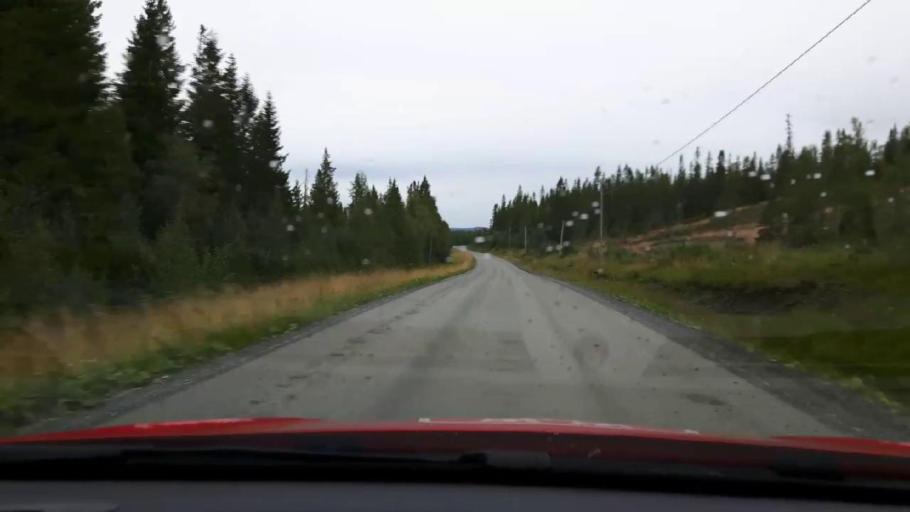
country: SE
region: Jaemtland
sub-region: Are Kommun
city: Are
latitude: 63.4820
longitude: 13.1497
